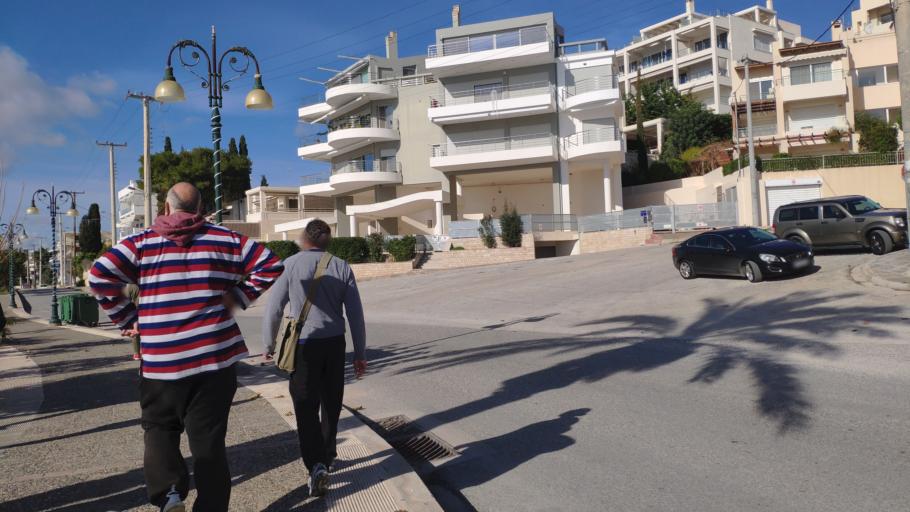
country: GR
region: Attica
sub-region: Nomarchia Anatolikis Attikis
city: Limin Mesoyaias
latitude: 37.8933
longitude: 24.0177
